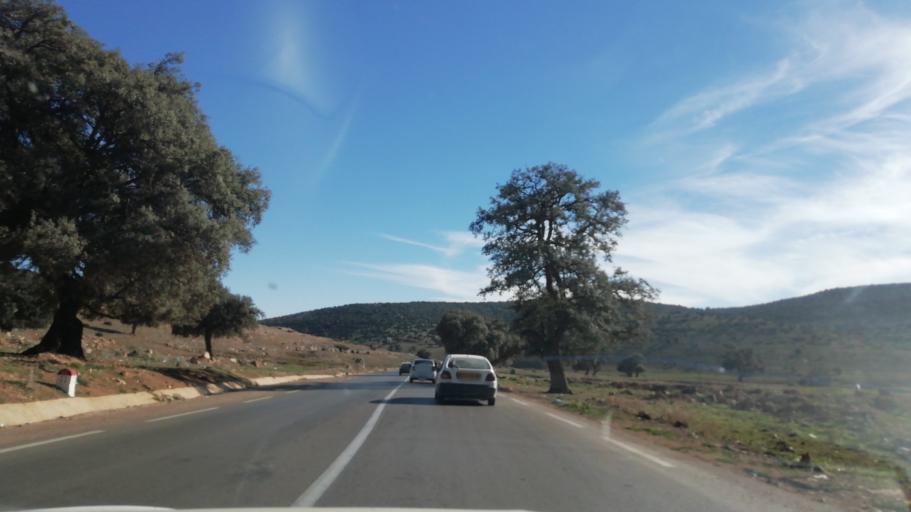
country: DZ
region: Tlemcen
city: Sebdou
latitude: 34.7201
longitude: -1.3387
